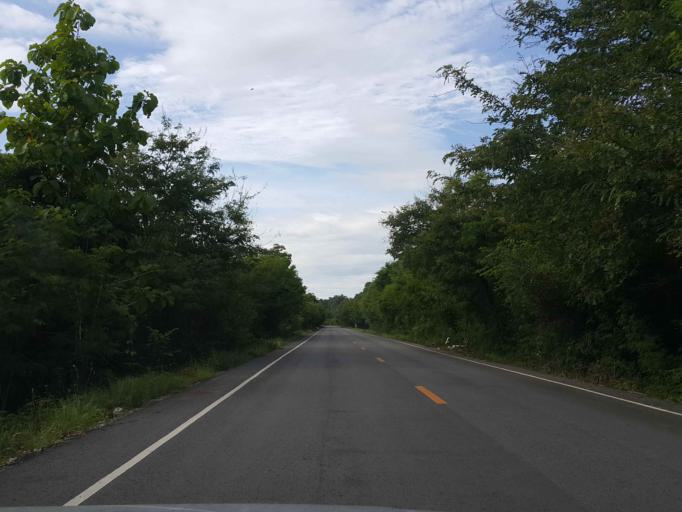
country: TH
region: Sukhothai
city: Thung Saliam
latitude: 17.2866
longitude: 99.5270
